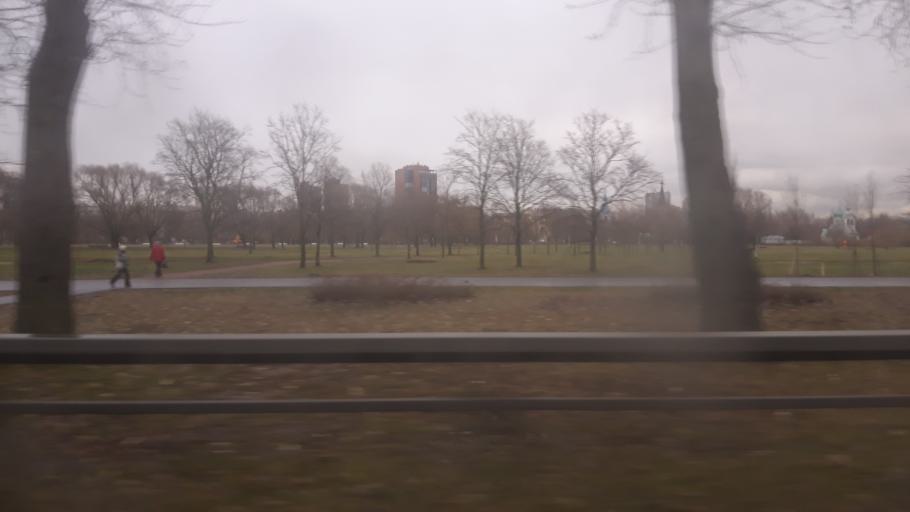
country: RU
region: St.-Petersburg
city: Kupchino
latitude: 59.8376
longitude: 30.3225
